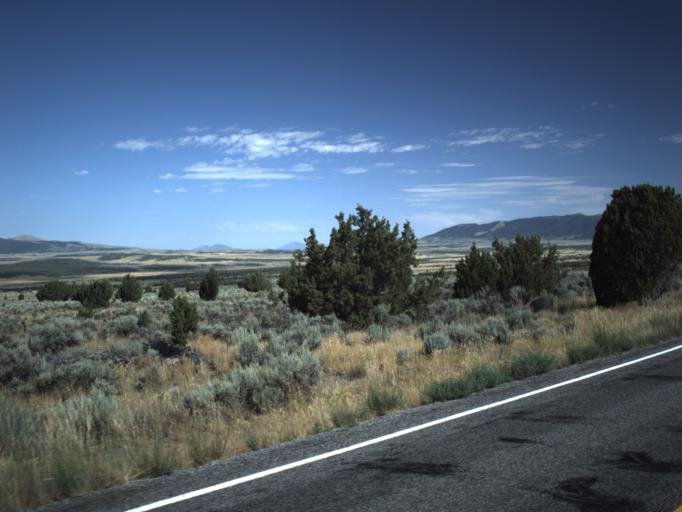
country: US
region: Utah
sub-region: Juab County
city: Mona
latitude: 39.8248
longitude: -112.1404
